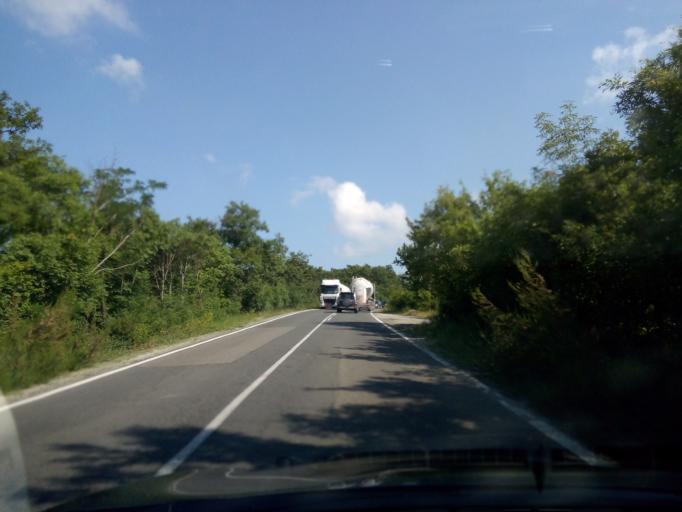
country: BG
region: Burgas
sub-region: Obshtina Nesebur
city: Sveti Vlas
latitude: 42.7497
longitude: 27.7533
